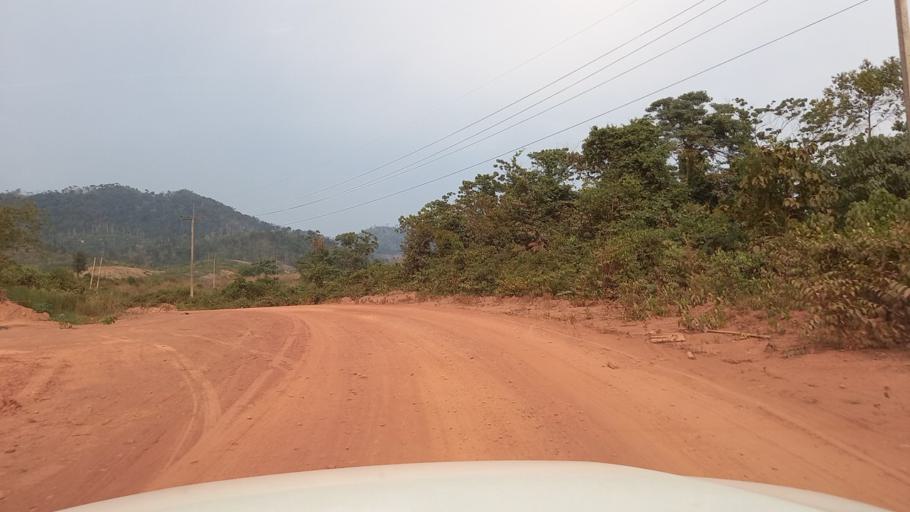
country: LA
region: Bolikhamxai
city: Bolikhan
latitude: 18.5362
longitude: 103.8079
